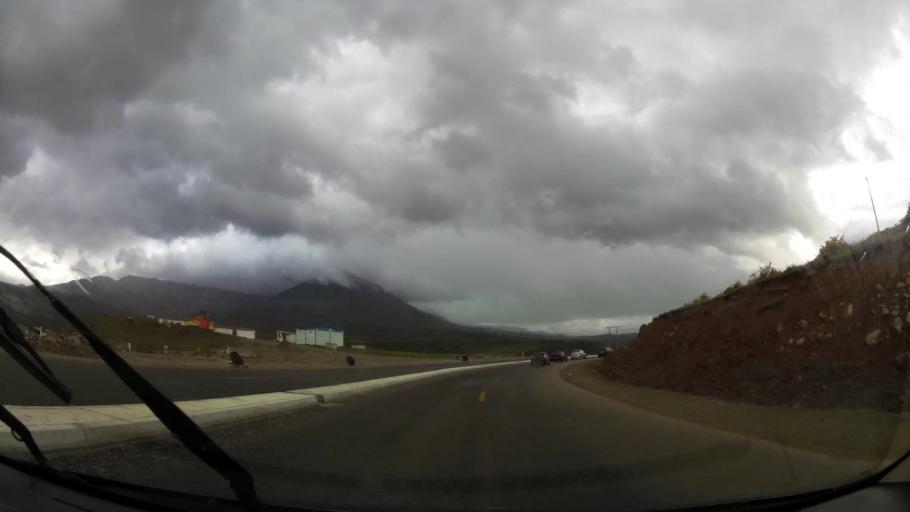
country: MA
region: Tanger-Tetouan
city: Chefchaouene
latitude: 35.2206
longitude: -5.3153
